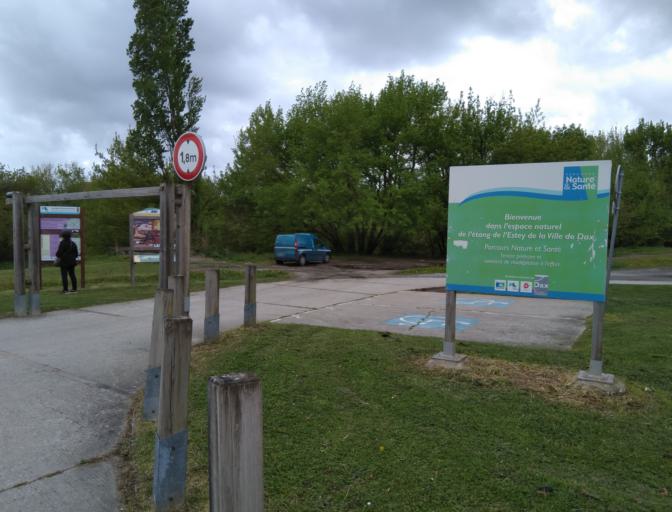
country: FR
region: Aquitaine
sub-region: Departement des Landes
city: Dax
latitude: 43.7146
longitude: -1.0499
